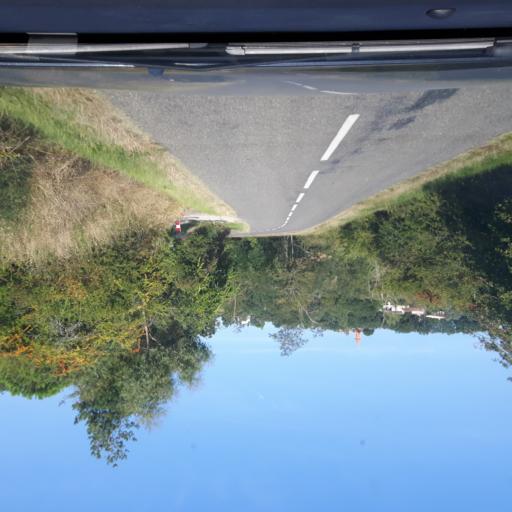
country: FR
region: Midi-Pyrenees
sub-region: Departement de la Haute-Garonne
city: Vacquiers
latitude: 43.7726
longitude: 1.4851
